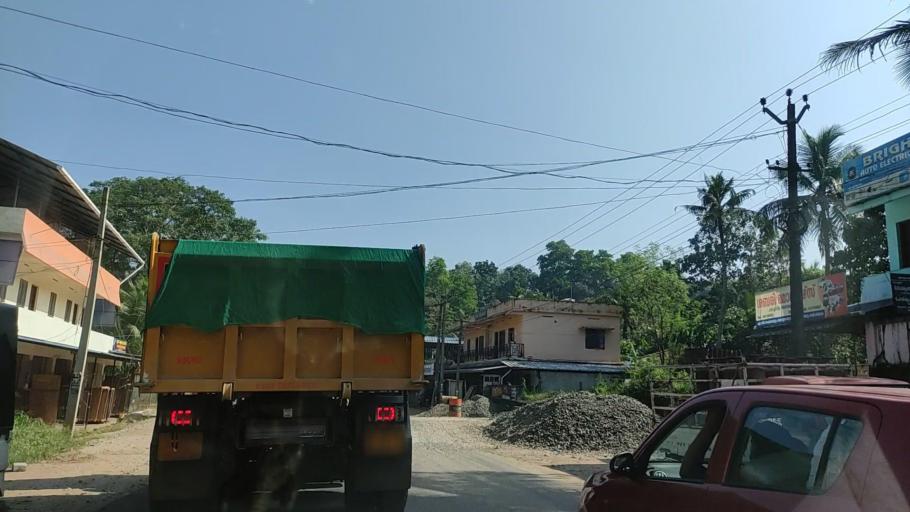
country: IN
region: Kerala
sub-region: Kollam
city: Punalur
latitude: 8.9193
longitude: 76.8940
